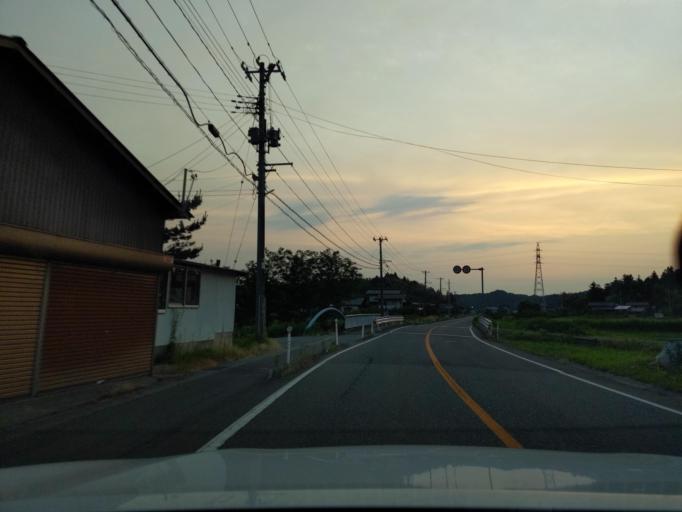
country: JP
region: Niigata
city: Kashiwazaki
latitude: 37.4444
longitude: 138.6518
